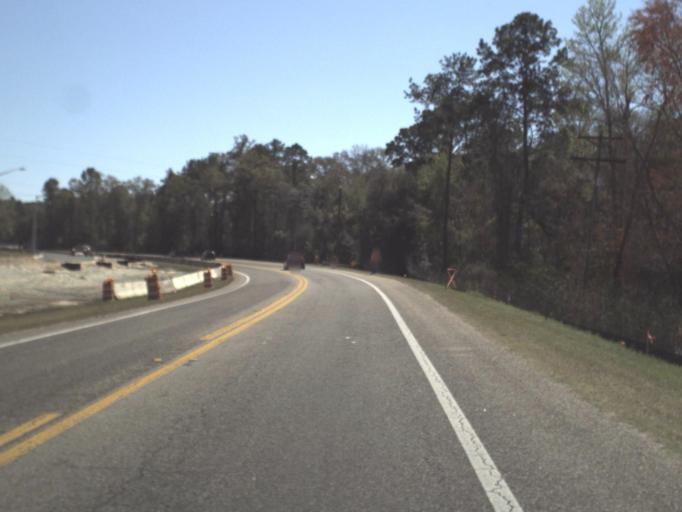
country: US
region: Florida
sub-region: Leon County
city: Tallahassee
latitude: 30.4243
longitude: -84.3529
